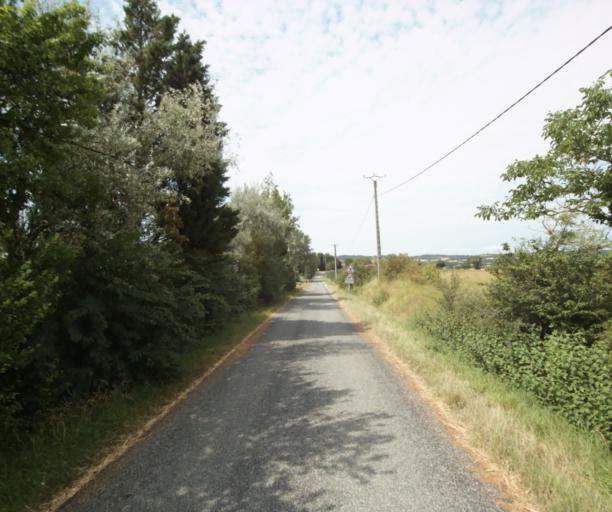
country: FR
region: Midi-Pyrenees
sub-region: Departement de la Haute-Garonne
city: Saint-Felix-Lauragais
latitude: 43.4227
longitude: 1.9115
